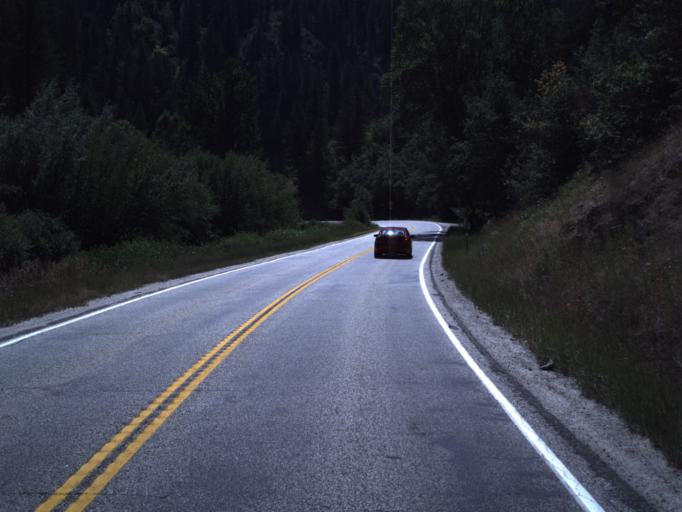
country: US
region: Utah
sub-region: Cache County
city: North Logan
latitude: 41.8164
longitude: -111.6178
